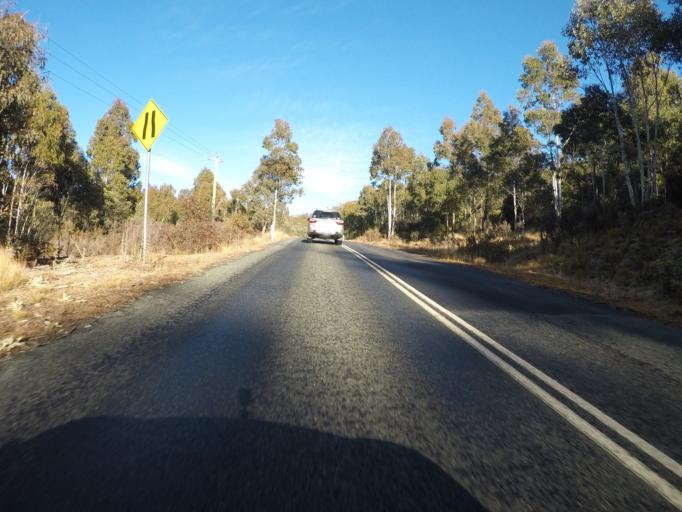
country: AU
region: Australian Capital Territory
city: Macarthur
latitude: -35.4928
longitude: 148.9253
